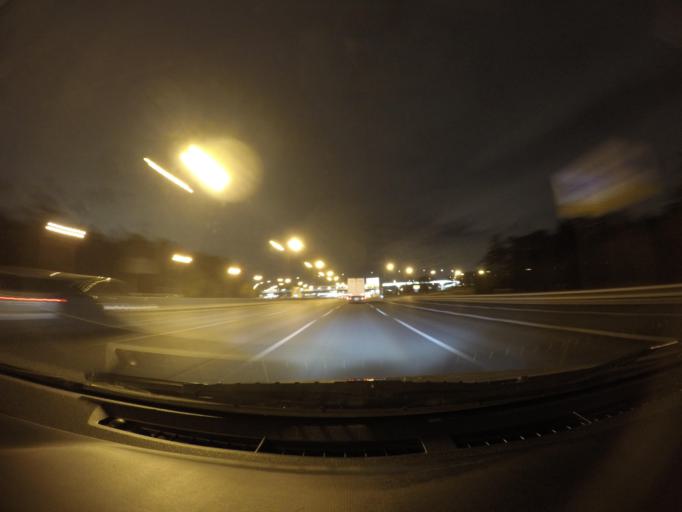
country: RU
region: Moscow
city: Zhulebino
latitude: 55.6826
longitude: 37.8325
